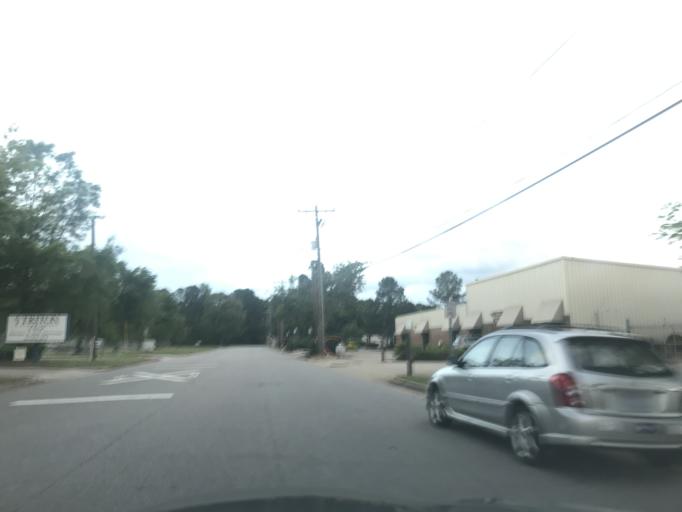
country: US
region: North Carolina
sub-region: Wake County
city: Raleigh
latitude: 35.8320
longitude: -78.6079
